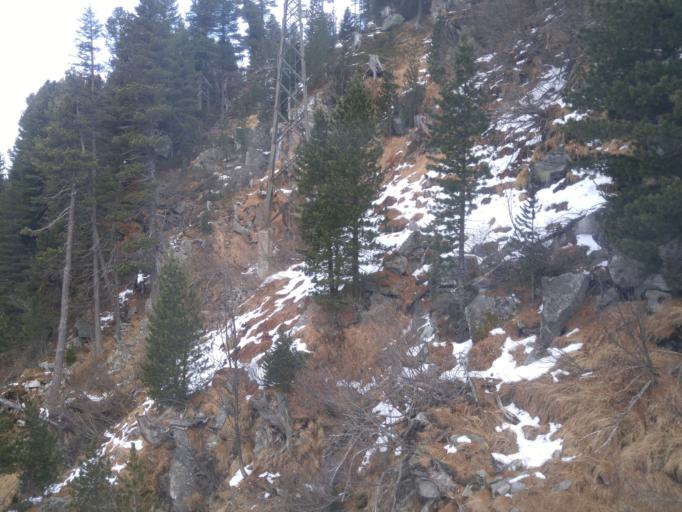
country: AT
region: Salzburg
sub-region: Politischer Bezirk Zell am See
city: Niedernsill
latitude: 47.1595
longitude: 12.6242
